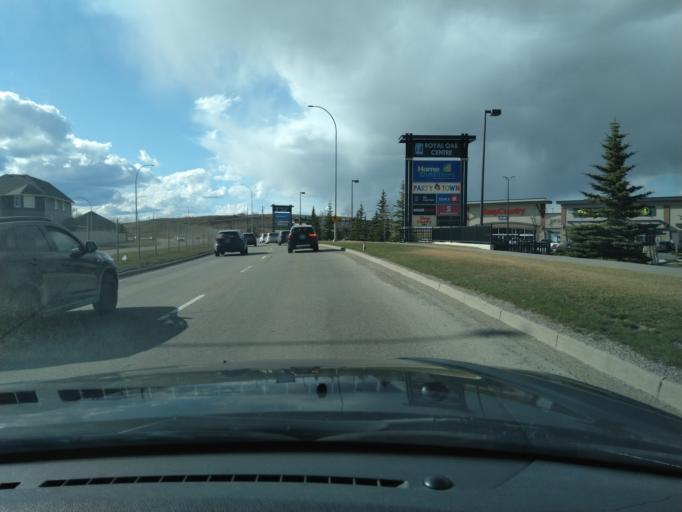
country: CA
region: Alberta
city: Calgary
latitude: 51.1529
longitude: -114.2165
